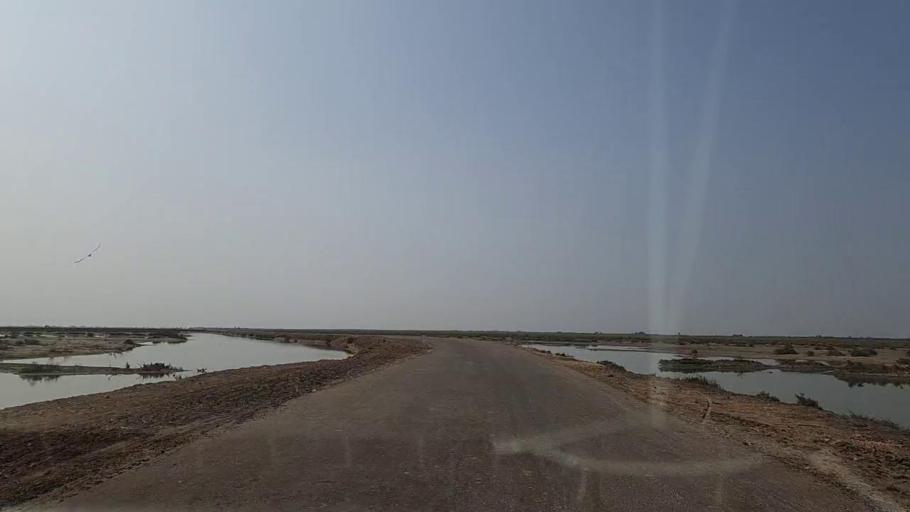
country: PK
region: Sindh
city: Chuhar Jamali
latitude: 24.2238
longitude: 67.8816
